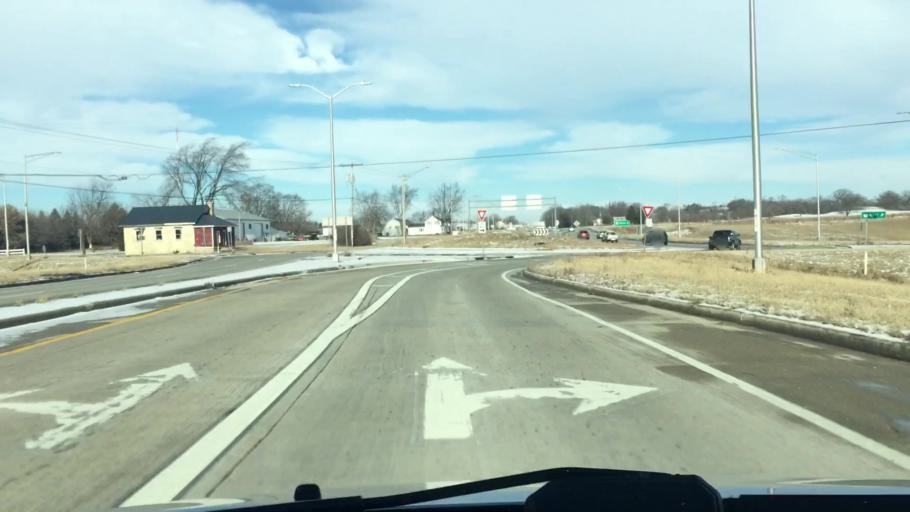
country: US
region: Wisconsin
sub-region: Waukesha County
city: Mukwonago
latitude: 42.9218
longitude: -88.3457
